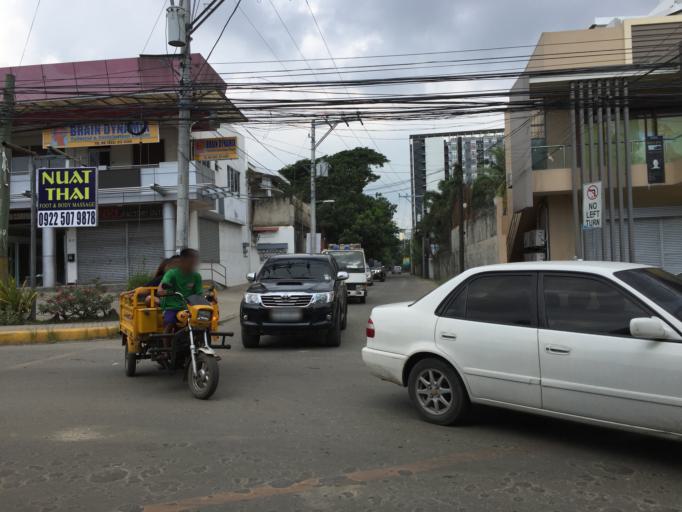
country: PH
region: Central Visayas
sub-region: Cebu City
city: Baugo
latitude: 10.3214
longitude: 123.9122
